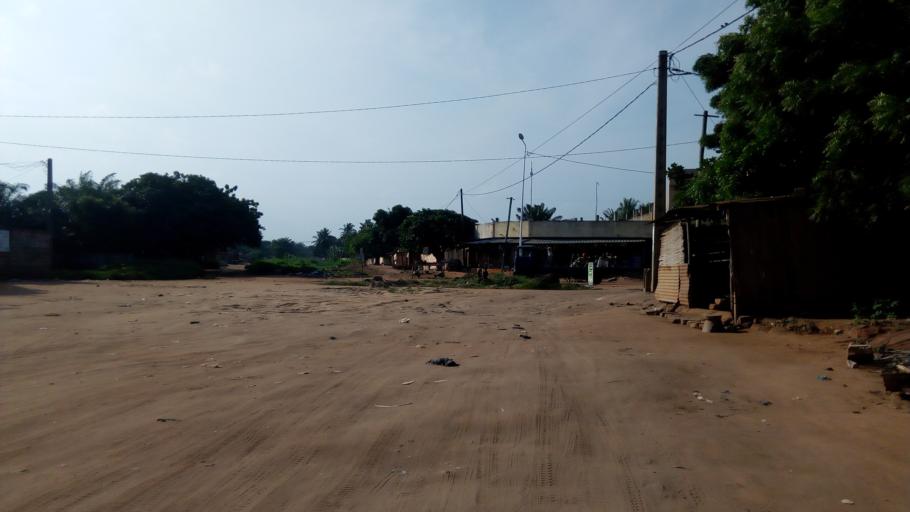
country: TG
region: Maritime
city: Lome
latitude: 6.1814
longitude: 1.1858
